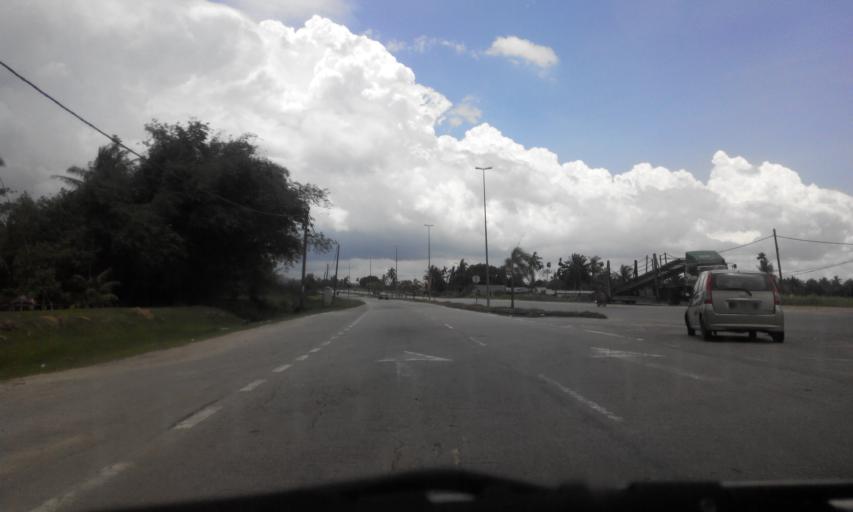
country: MY
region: Perak
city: Parit Buntar
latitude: 5.1284
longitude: 100.5029
